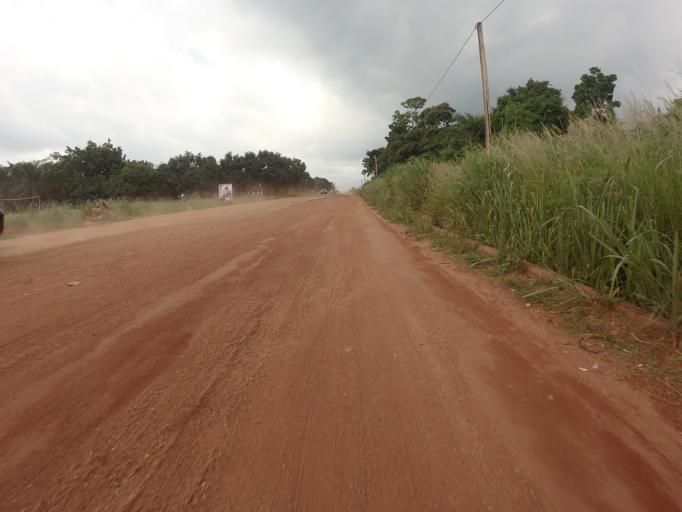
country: TG
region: Plateaux
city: Kpalime
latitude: 6.9161
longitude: 0.4571
